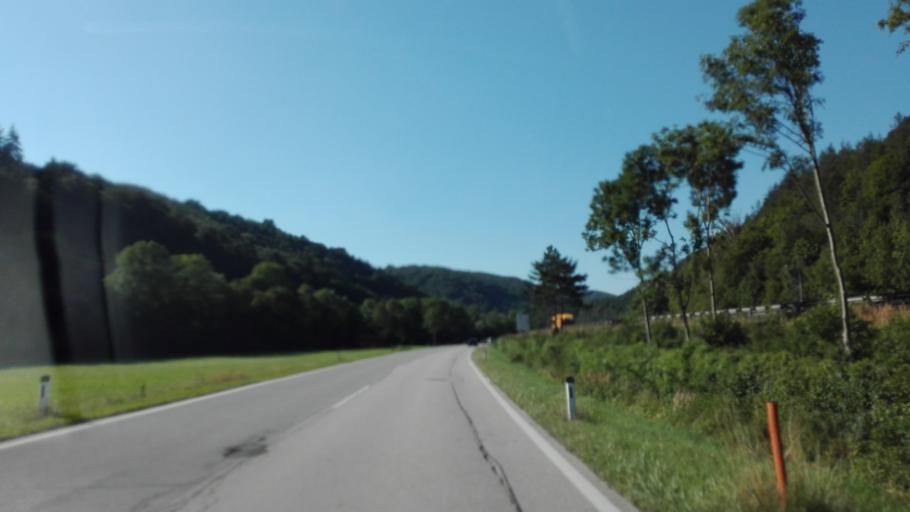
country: AT
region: Lower Austria
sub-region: Politischer Bezirk Baden
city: Alland
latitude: 48.0751
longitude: 16.0539
